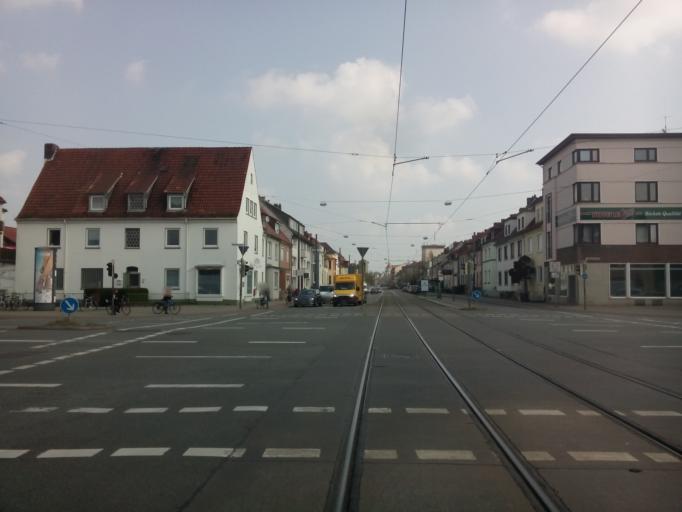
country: DE
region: Bremen
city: Bremen
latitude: 53.0671
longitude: 8.7822
